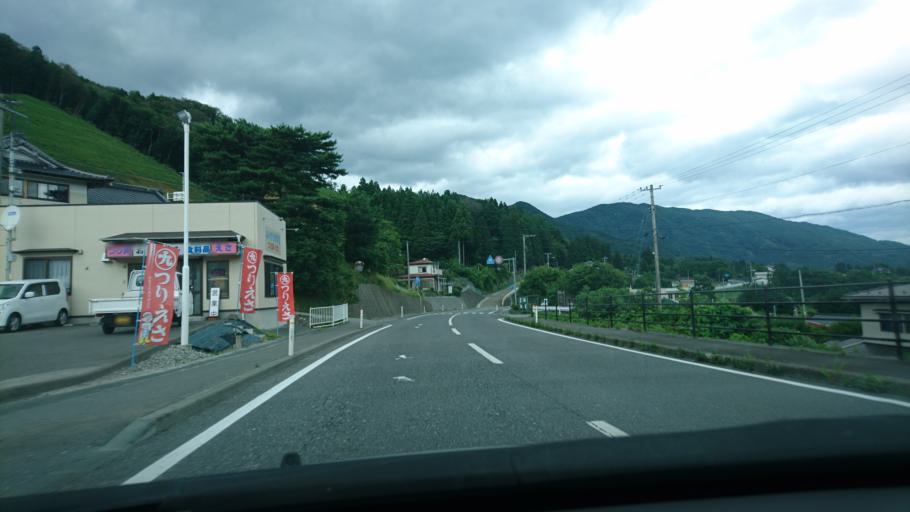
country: JP
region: Iwate
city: Kamaishi
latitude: 39.1510
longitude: 141.8321
